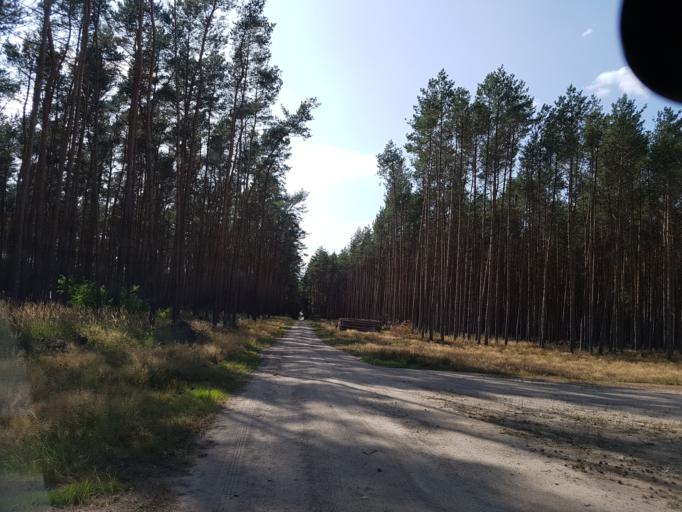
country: DE
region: Brandenburg
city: Treuenbrietzen
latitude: 52.0149
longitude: 12.8512
